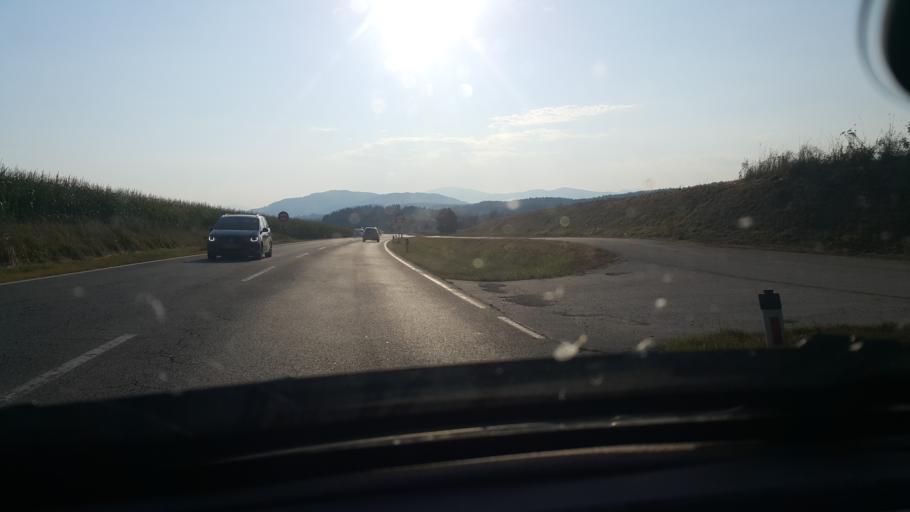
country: AT
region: Carinthia
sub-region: Politischer Bezirk Feldkirchen
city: Glanegg
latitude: 46.6703
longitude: 14.2363
